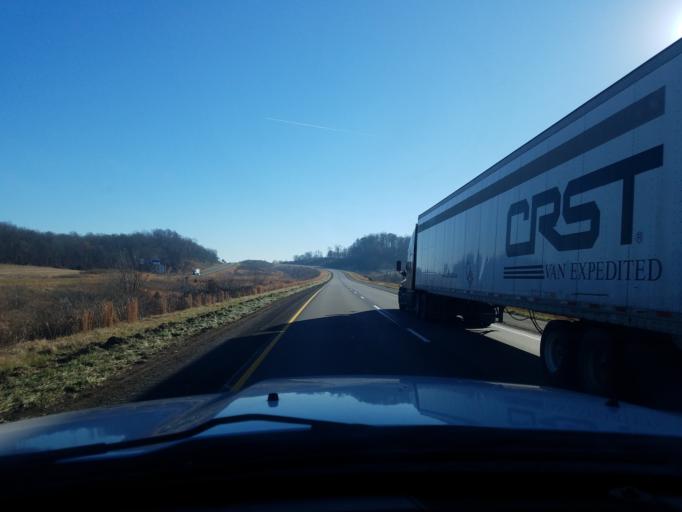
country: US
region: Indiana
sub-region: Dubois County
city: Ferdinand
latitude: 38.2039
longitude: -86.8435
